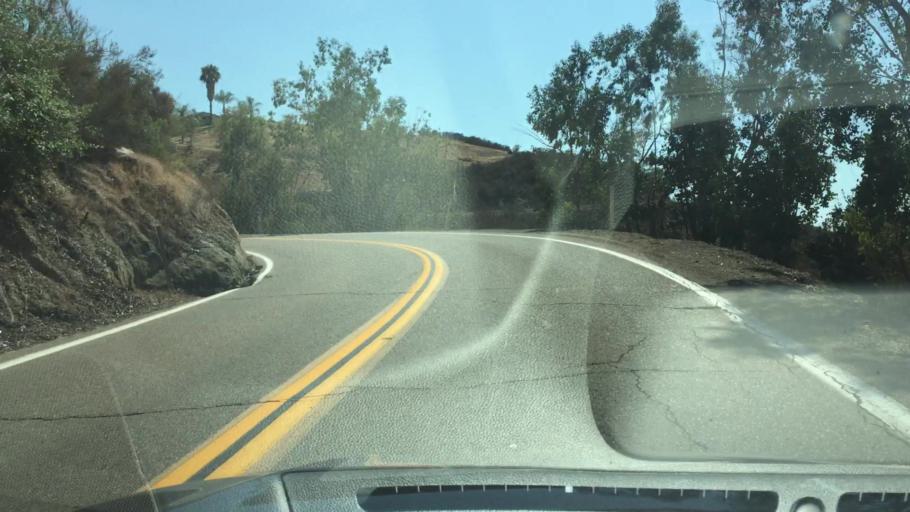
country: US
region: California
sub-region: San Diego County
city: Jamul
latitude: 32.7359
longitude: -116.8159
